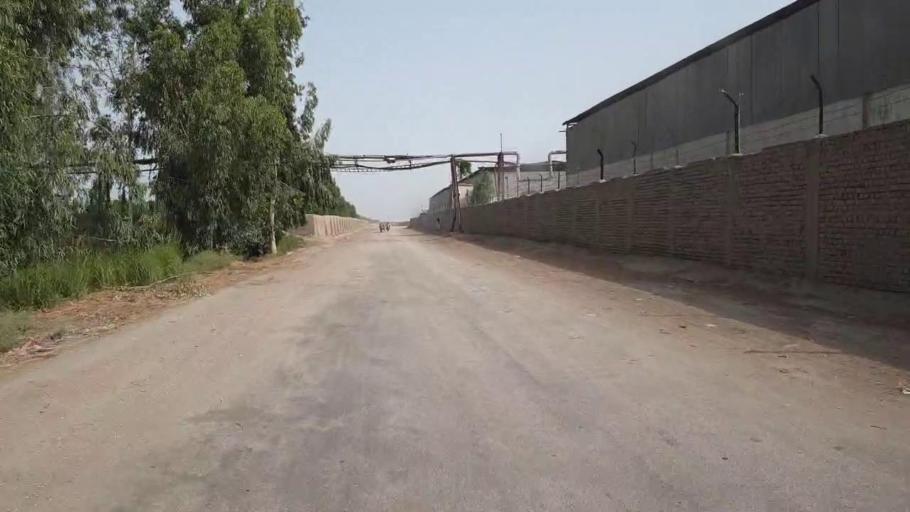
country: PK
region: Sindh
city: Daulatpur
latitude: 26.5583
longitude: 67.9888
